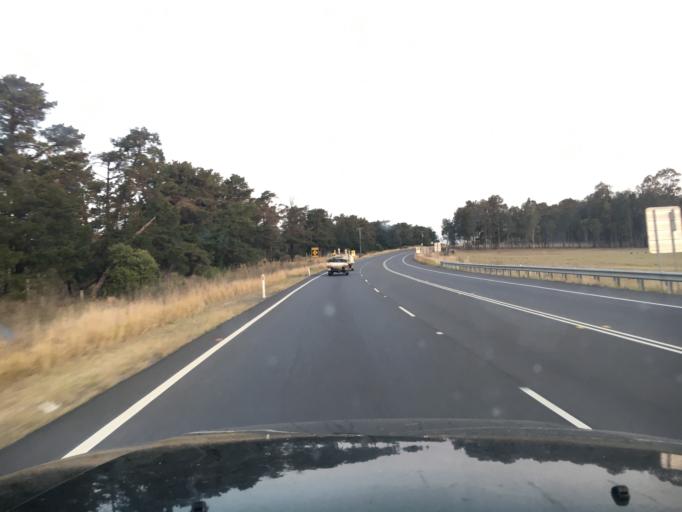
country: AU
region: New South Wales
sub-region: Cessnock
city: Greta
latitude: -32.6876
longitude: 151.4005
